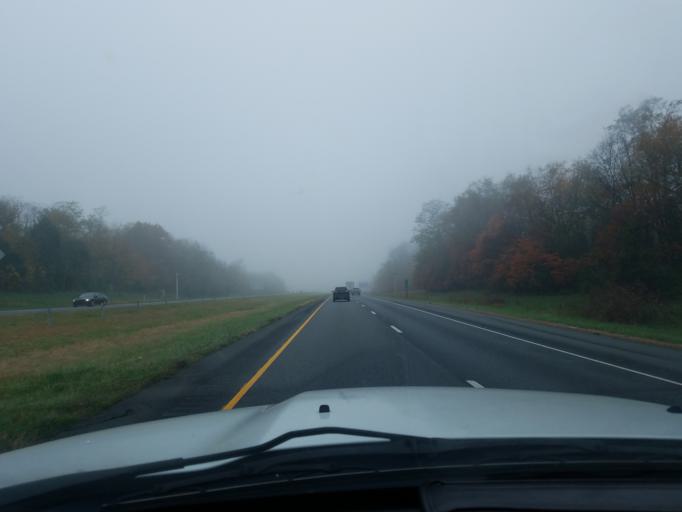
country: US
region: Indiana
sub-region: Floyd County
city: Georgetown
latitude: 38.2830
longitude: -85.9263
